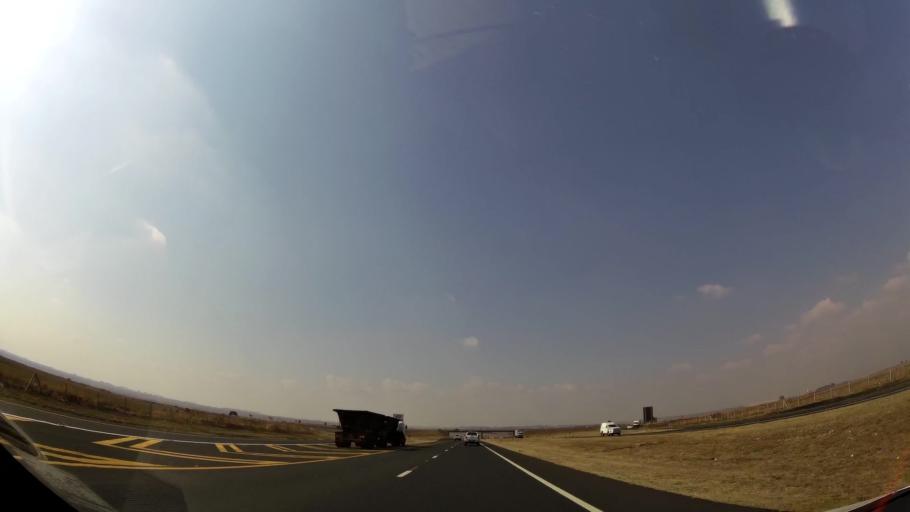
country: ZA
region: Gauteng
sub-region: Ekurhuleni Metropolitan Municipality
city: Springs
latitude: -26.1605
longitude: 28.4405
